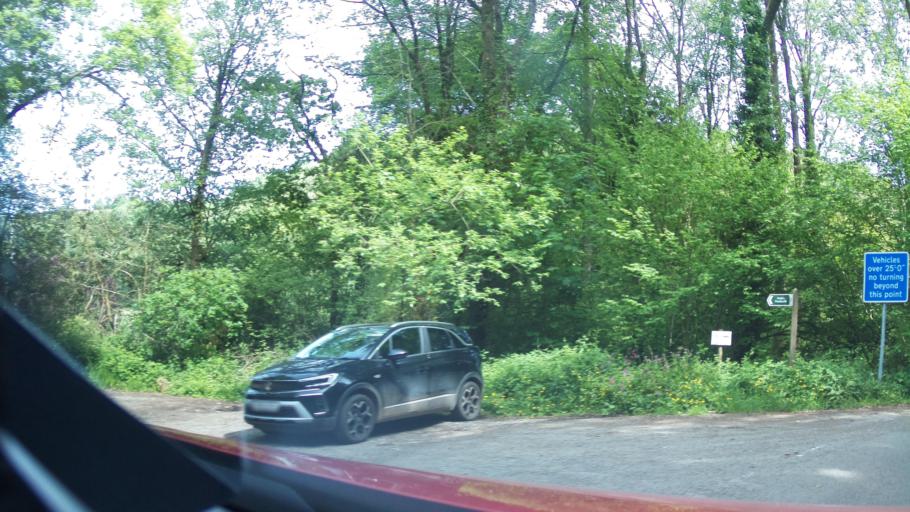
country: GB
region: England
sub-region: Devon
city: South Brent
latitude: 50.3688
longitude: -3.7891
